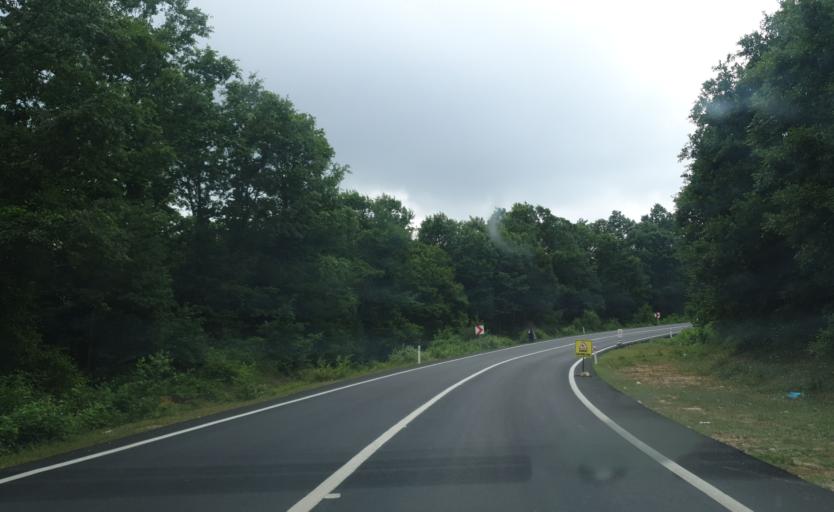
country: TR
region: Kirklareli
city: Salmydessus
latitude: 41.5865
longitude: 28.0683
